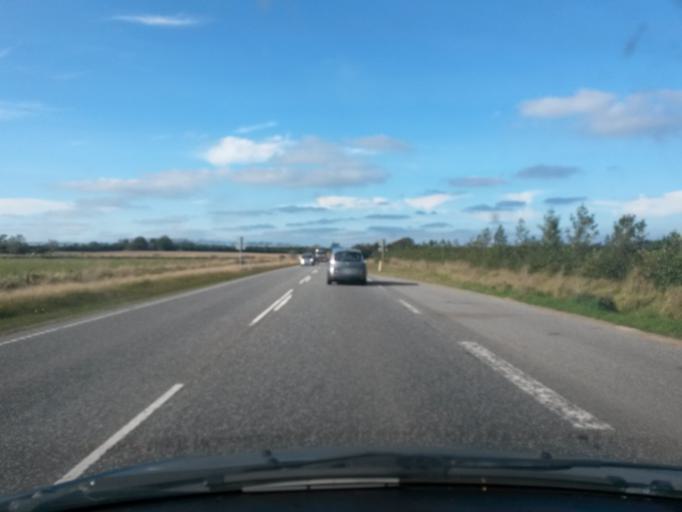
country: DK
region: Central Jutland
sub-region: Herning Kommune
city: Avlum
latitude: 56.2675
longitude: 8.7707
